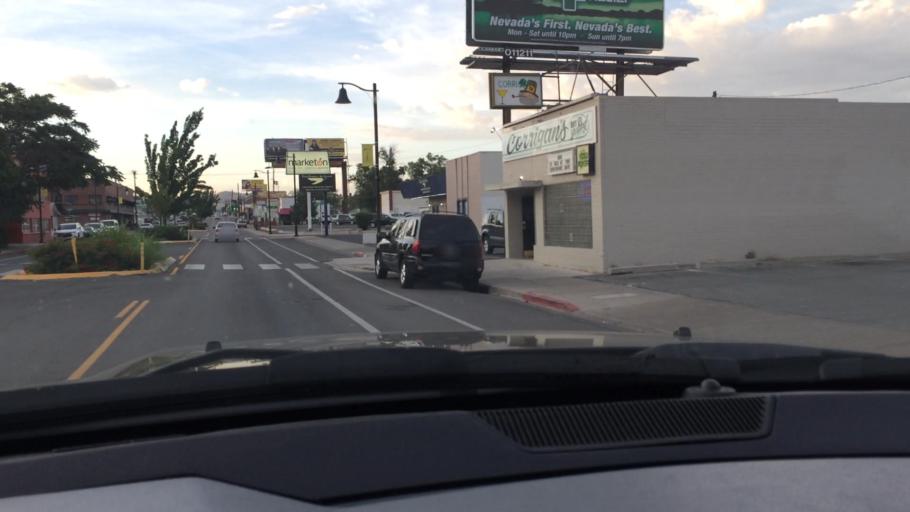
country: US
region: Nevada
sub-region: Washoe County
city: Reno
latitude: 39.5090
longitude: -119.8030
